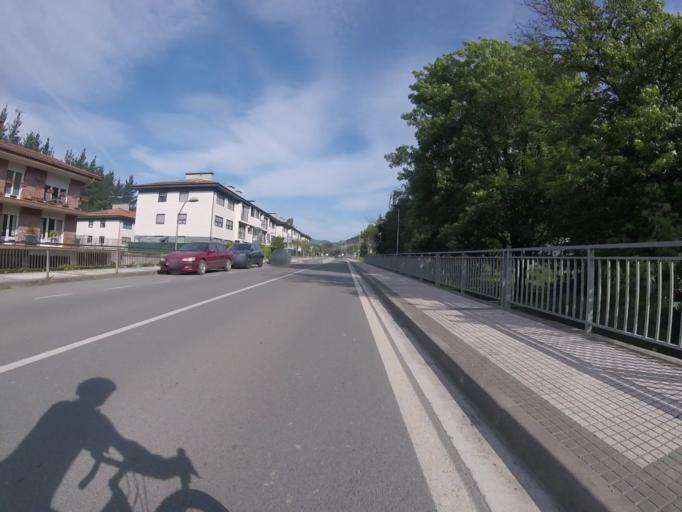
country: ES
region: Basque Country
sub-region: Provincia de Guipuzcoa
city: Gabiria
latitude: 43.0646
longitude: -2.2761
